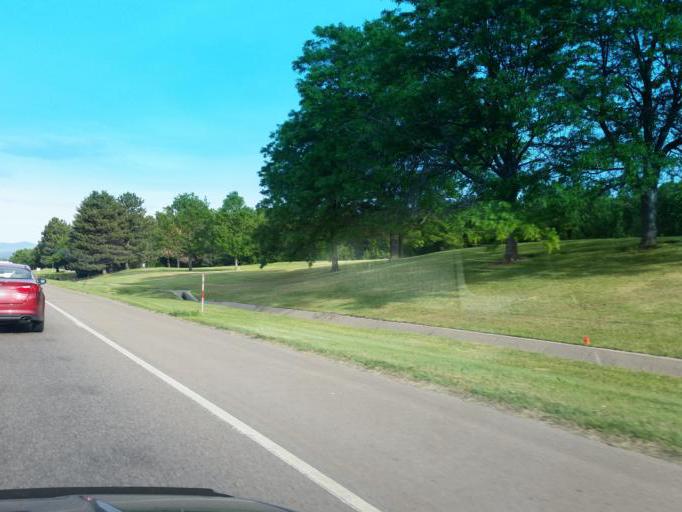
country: US
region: Colorado
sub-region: Larimer County
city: Fort Collins
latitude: 40.5235
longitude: -105.0134
